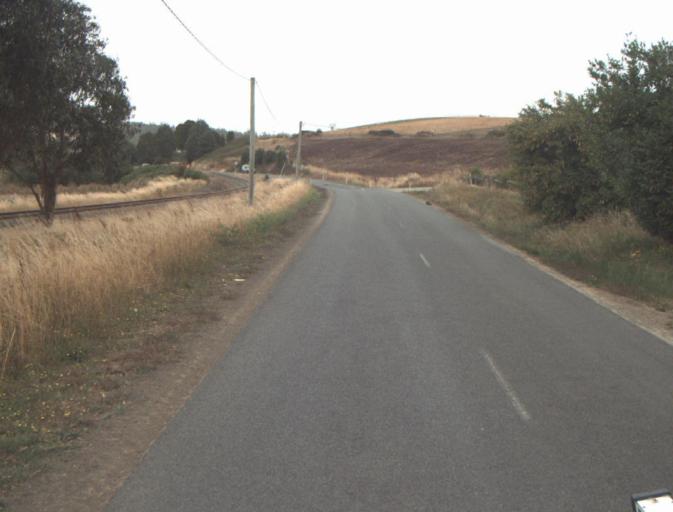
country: AU
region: Tasmania
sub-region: Launceston
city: Mayfield
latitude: -41.1813
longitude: 147.2235
